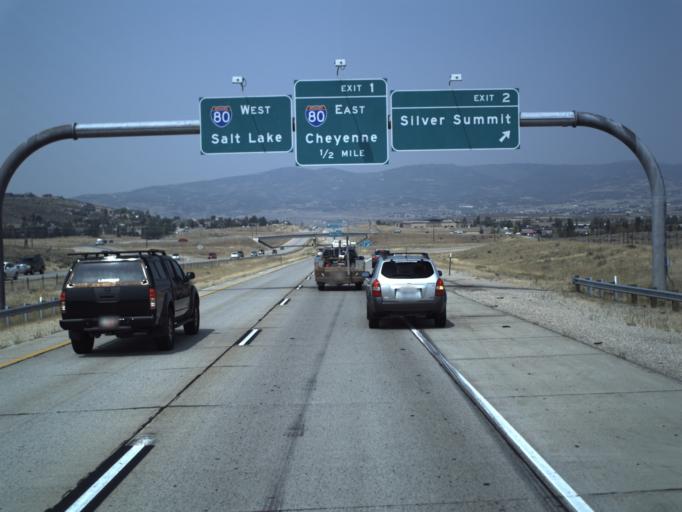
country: US
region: Utah
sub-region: Summit County
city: Snyderville
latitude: 40.7134
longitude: -111.4834
